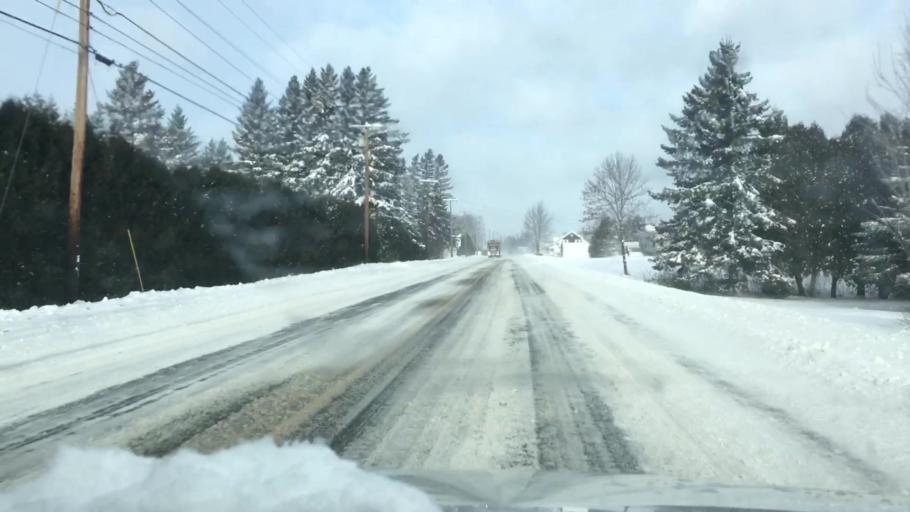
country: US
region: Maine
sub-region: Aroostook County
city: Van Buren
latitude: 47.1806
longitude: -67.9517
